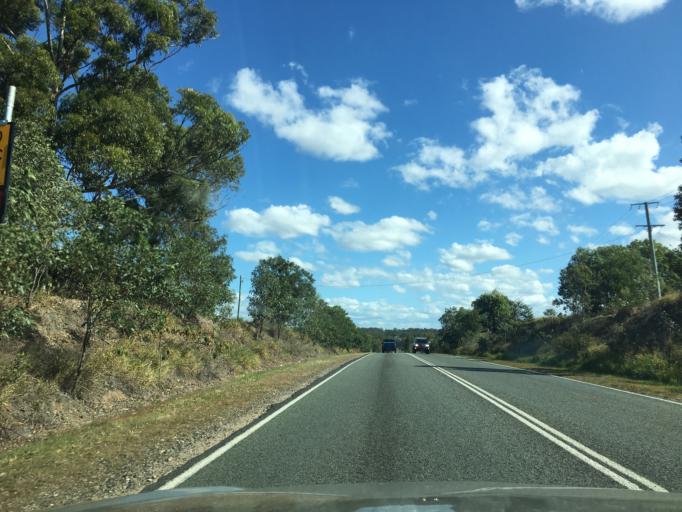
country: AU
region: Queensland
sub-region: Logan
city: Logan Reserve
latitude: -27.7412
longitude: 153.1273
